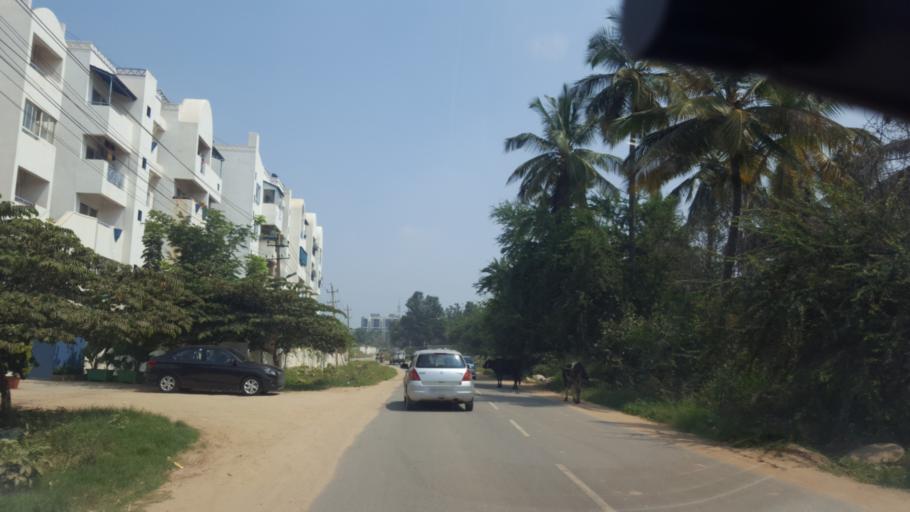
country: IN
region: Karnataka
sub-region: Bangalore Urban
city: Bangalore
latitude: 12.9384
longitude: 77.7161
